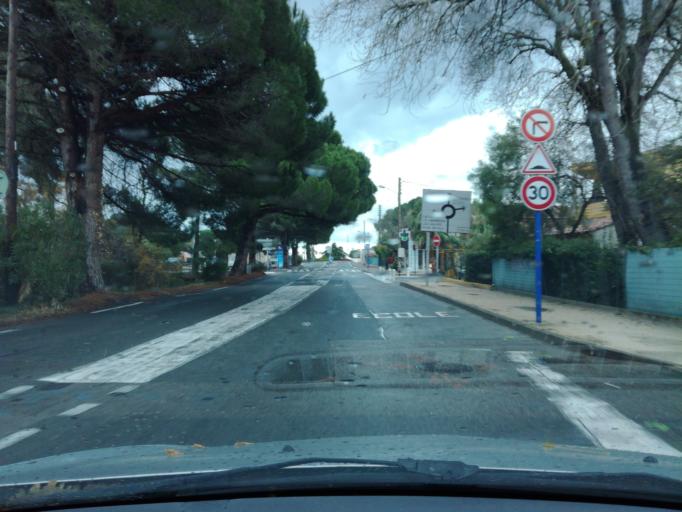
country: FR
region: Provence-Alpes-Cote d'Azur
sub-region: Departement du Var
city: Hyeres
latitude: 43.1069
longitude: 6.1748
